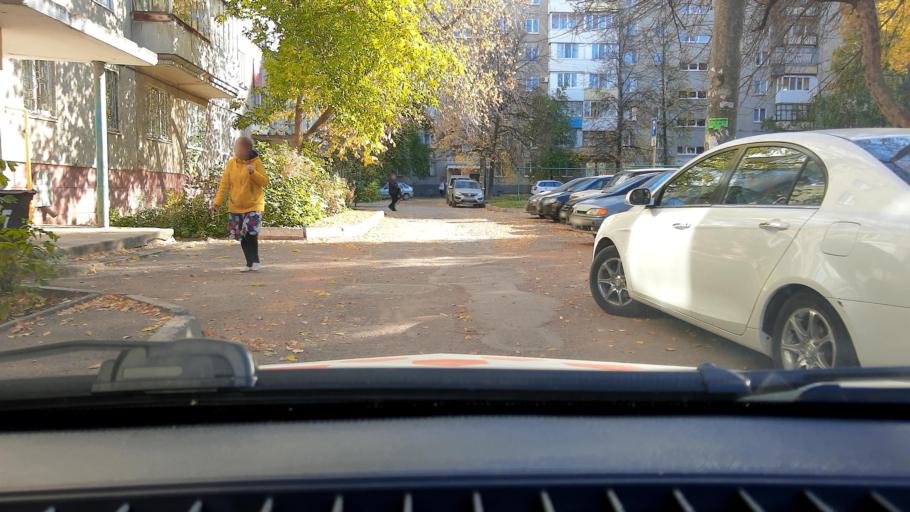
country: RU
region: Bashkortostan
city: Ufa
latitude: 54.8092
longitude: 56.1330
